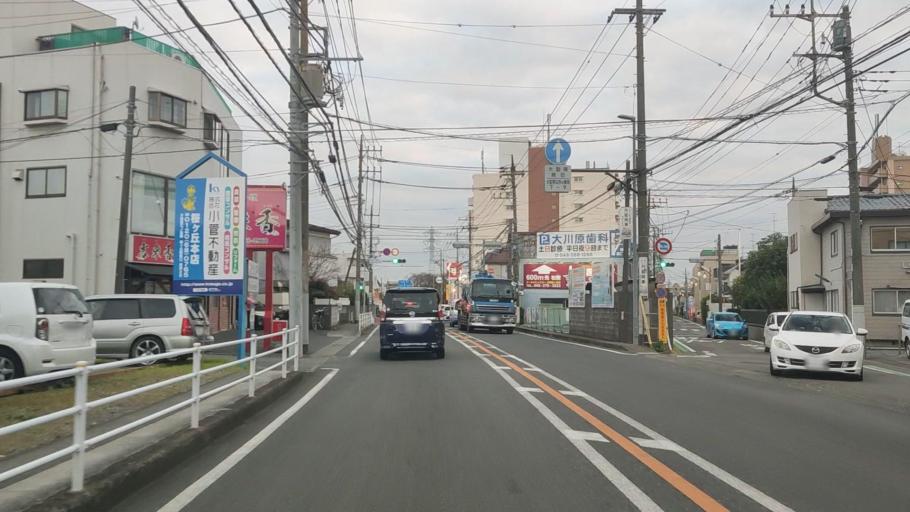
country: JP
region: Kanagawa
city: Minami-rinkan
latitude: 35.4532
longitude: 139.4669
